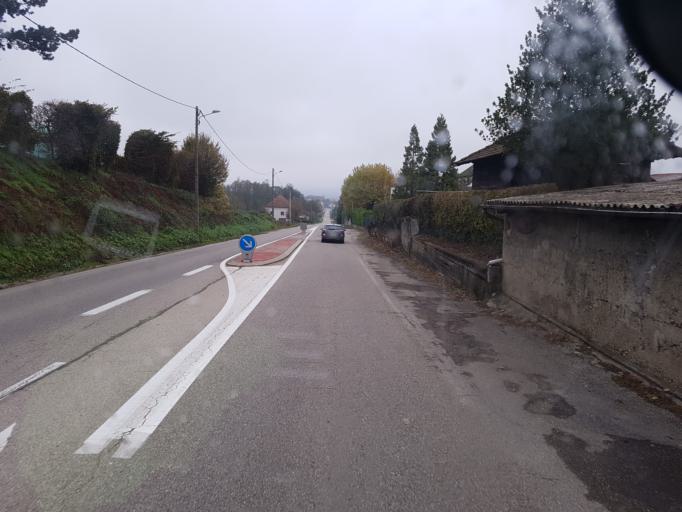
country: FR
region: Rhone-Alpes
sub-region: Departement de l'Isere
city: Chimilin
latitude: 45.5761
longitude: 5.6035
